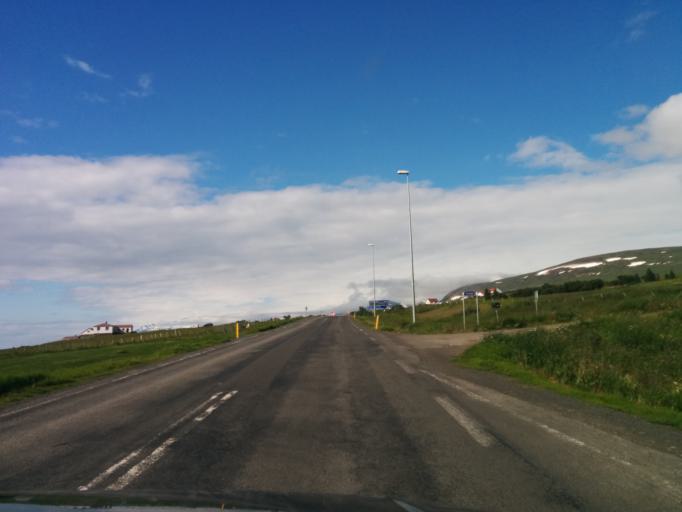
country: IS
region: Northeast
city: Akureyri
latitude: 65.7504
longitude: -18.0747
